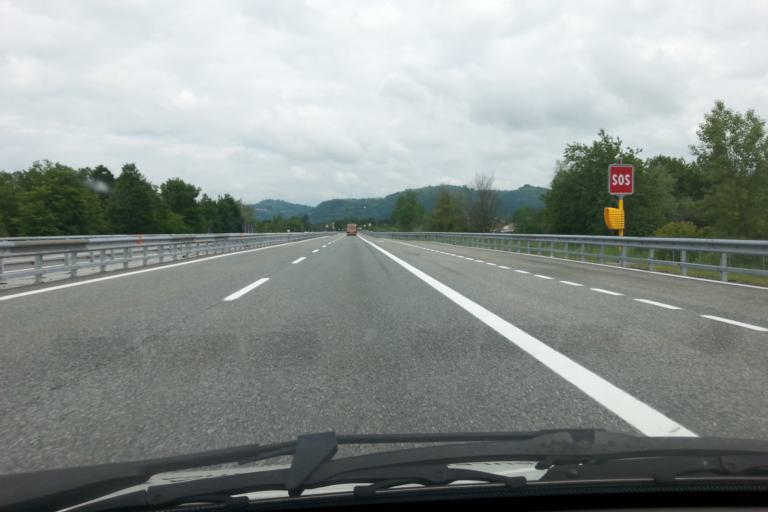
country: IT
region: Piedmont
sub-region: Provincia di Cuneo
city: Lesegno
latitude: 44.4057
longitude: 7.9708
